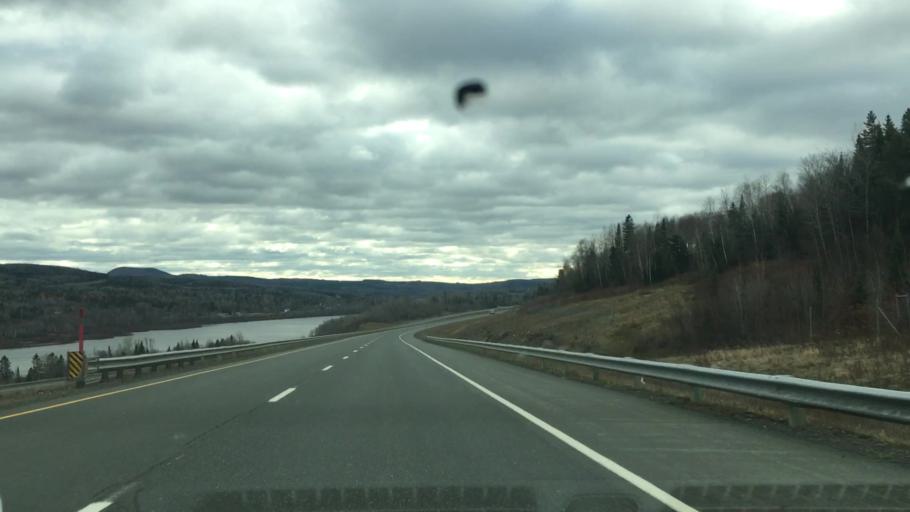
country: US
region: Maine
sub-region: Aroostook County
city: Fort Fairfield
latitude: 46.6831
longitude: -67.7332
